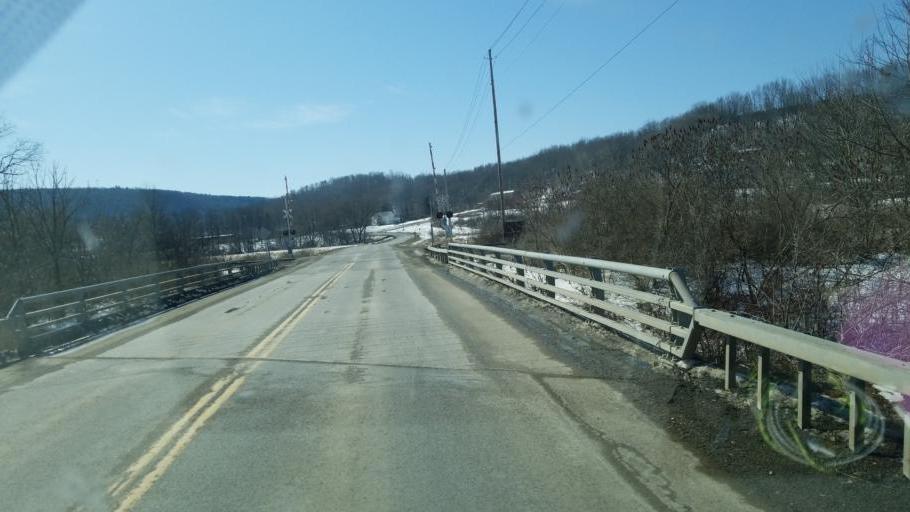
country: US
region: New York
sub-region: Steuben County
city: Hornell
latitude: 42.3757
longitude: -77.6877
